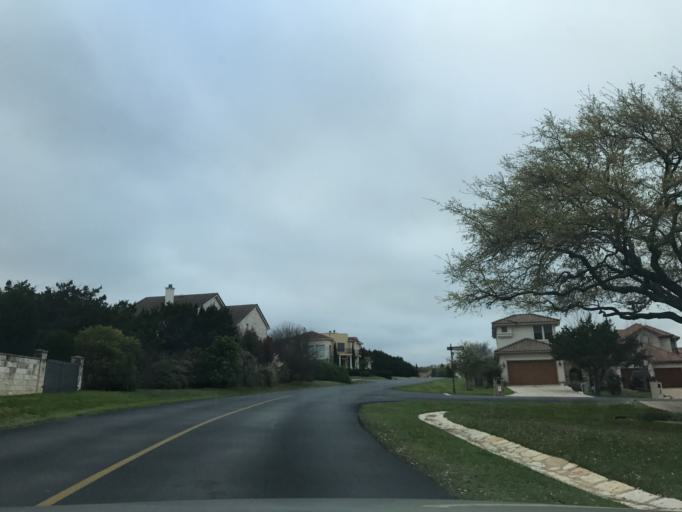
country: US
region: Texas
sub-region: Travis County
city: The Hills
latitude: 30.3398
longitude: -97.9915
